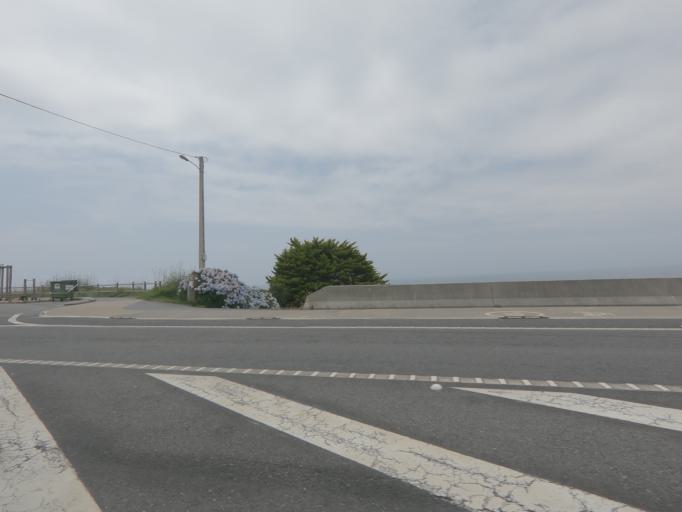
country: ES
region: Galicia
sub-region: Provincia de Pontevedra
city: Oia
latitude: 41.9884
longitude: -8.8834
